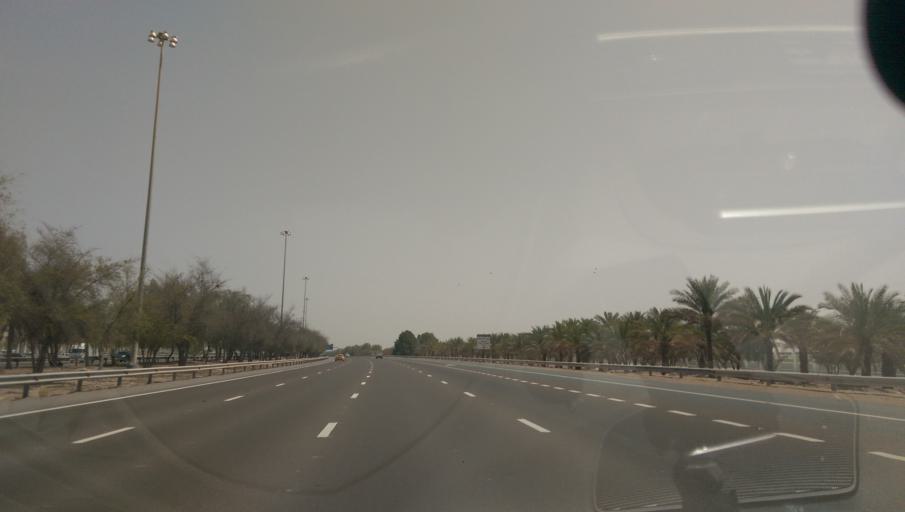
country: AE
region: Abu Dhabi
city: Abu Dhabi
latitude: 24.5220
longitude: 54.6911
